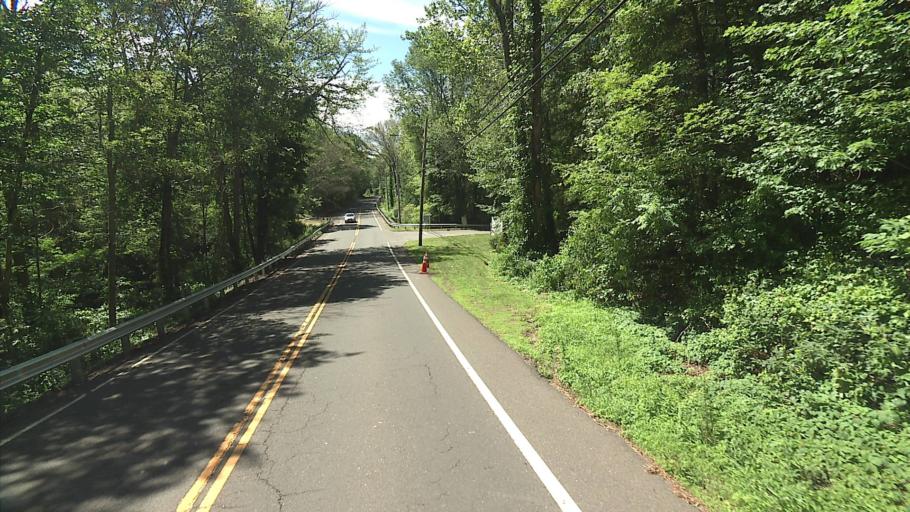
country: US
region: Connecticut
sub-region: New Haven County
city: North Branford
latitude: 41.3576
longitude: -72.7210
